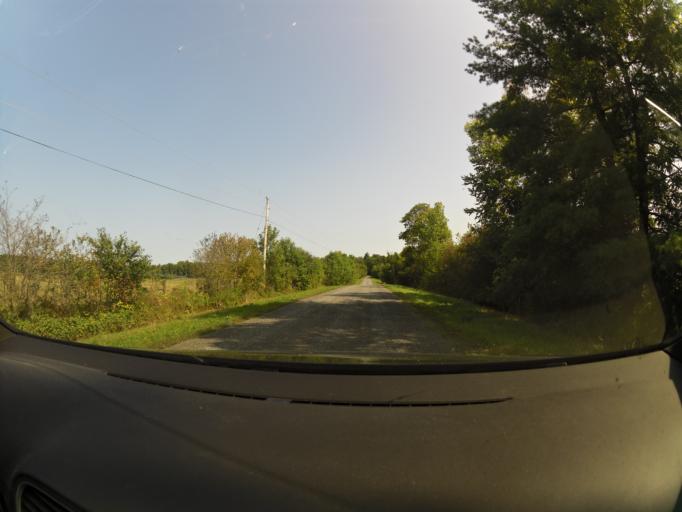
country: CA
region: Ontario
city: Arnprior
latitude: 45.5023
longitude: -76.2071
